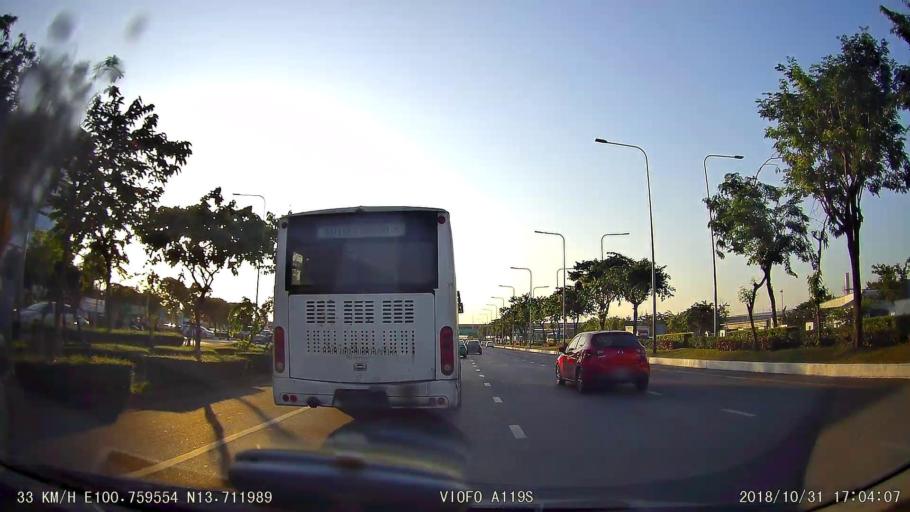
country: TH
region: Bangkok
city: Lat Krabang
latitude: 13.7120
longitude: 100.7596
